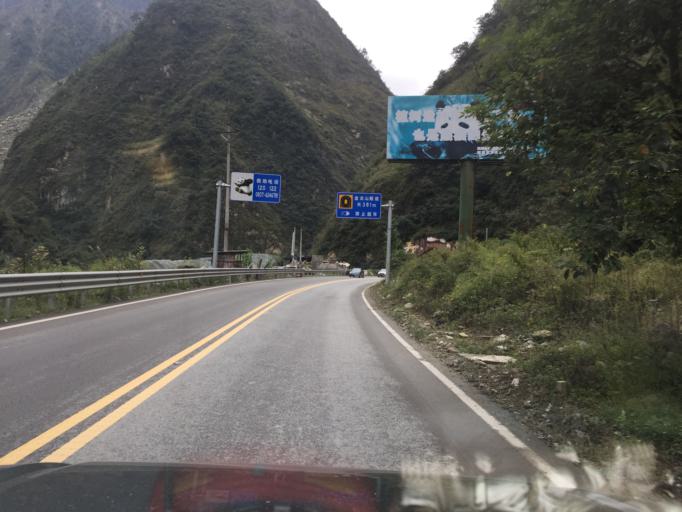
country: CN
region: Sichuan
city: Guangsheng
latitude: 31.0615
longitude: 103.4062
